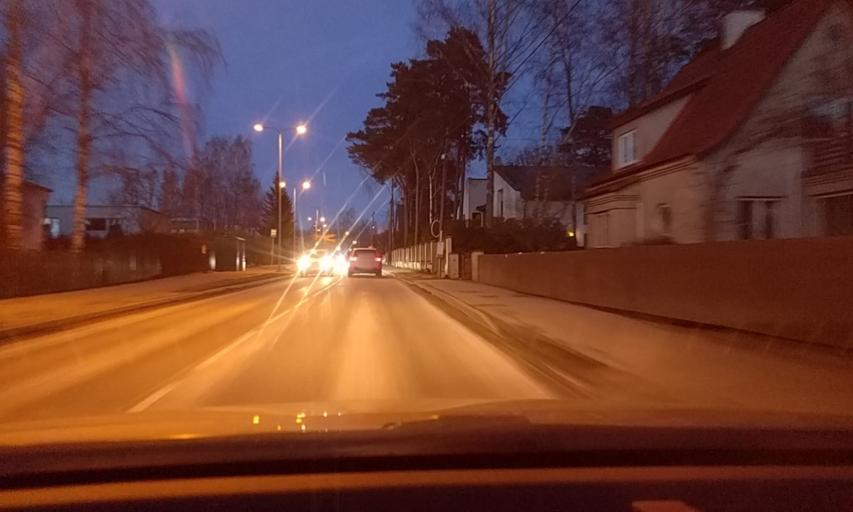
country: EE
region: Harju
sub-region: Viimsi vald
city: Viimsi
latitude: 59.4782
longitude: 24.8482
